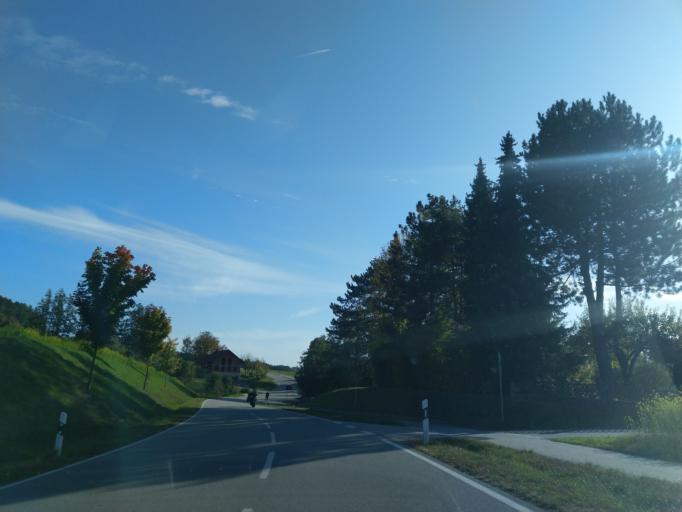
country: DE
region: Bavaria
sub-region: Lower Bavaria
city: Bernried
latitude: 48.9135
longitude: 12.8821
